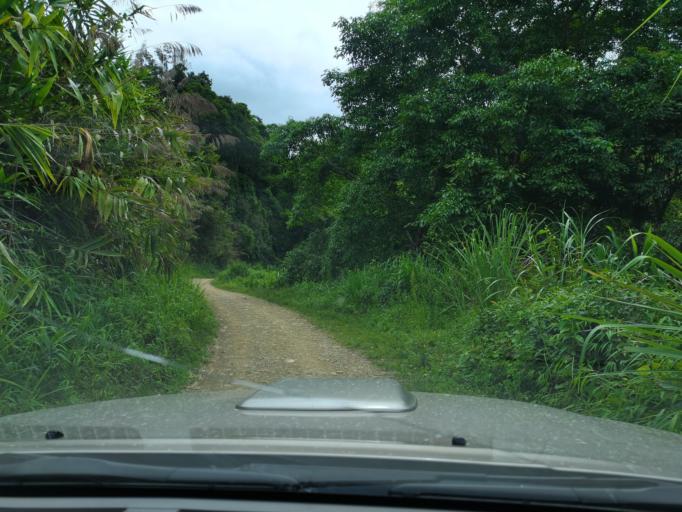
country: LA
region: Phongsali
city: Phongsali
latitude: 21.6753
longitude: 102.1888
